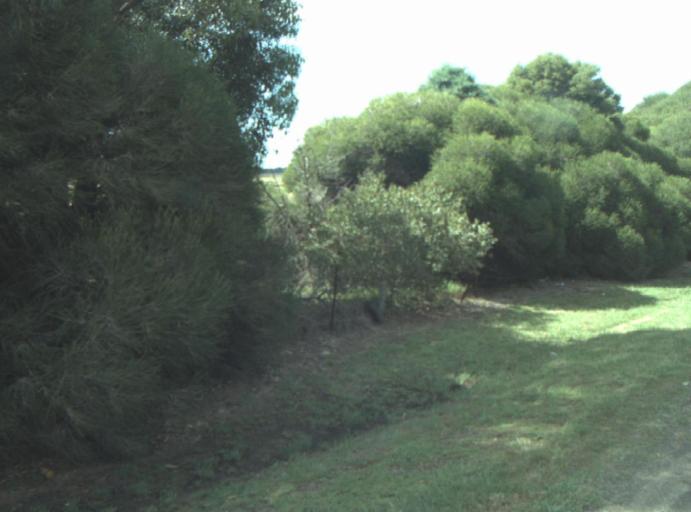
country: AU
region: Victoria
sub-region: Greater Geelong
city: Lara
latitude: -38.0466
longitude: 144.4293
